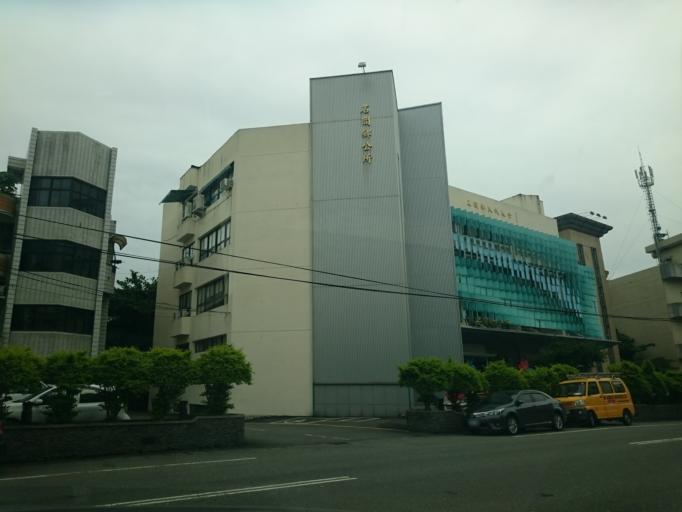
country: TW
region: Taiwan
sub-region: Nantou
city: Nantou
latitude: 23.8383
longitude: 120.7026
